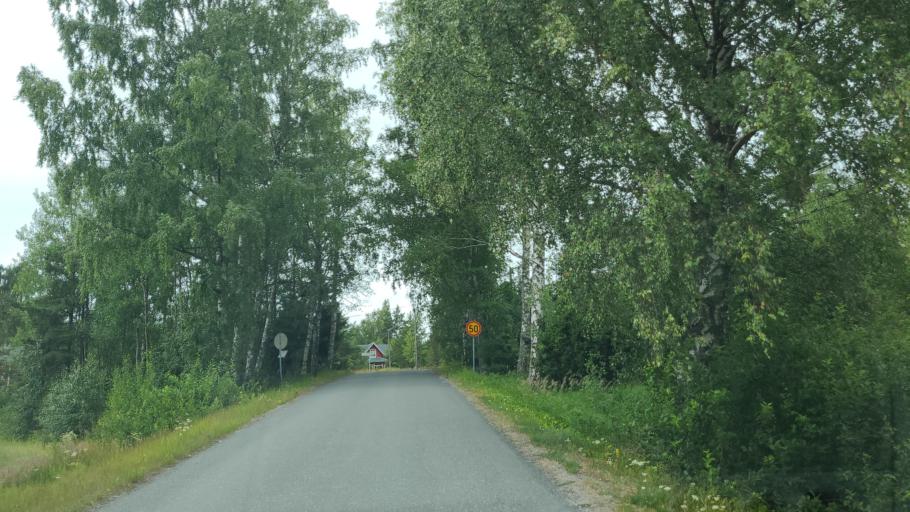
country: FI
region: Varsinais-Suomi
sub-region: Aboland-Turunmaa
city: Dragsfjaerd
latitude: 60.0974
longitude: 22.4327
